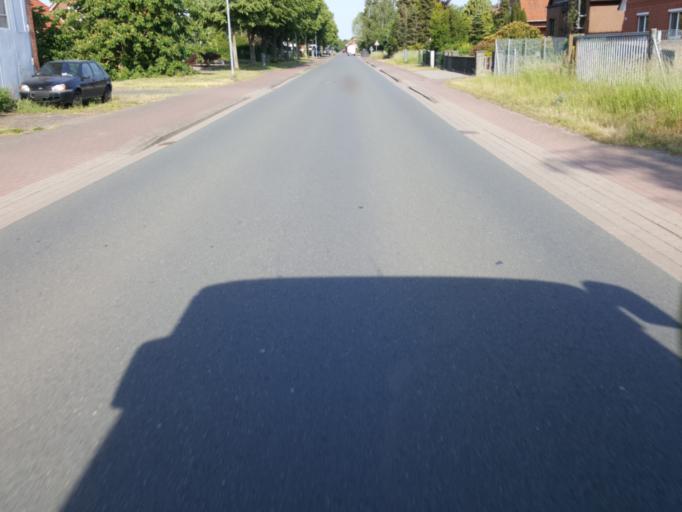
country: DE
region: Lower Saxony
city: Landesbergen
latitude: 52.5597
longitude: 9.1340
